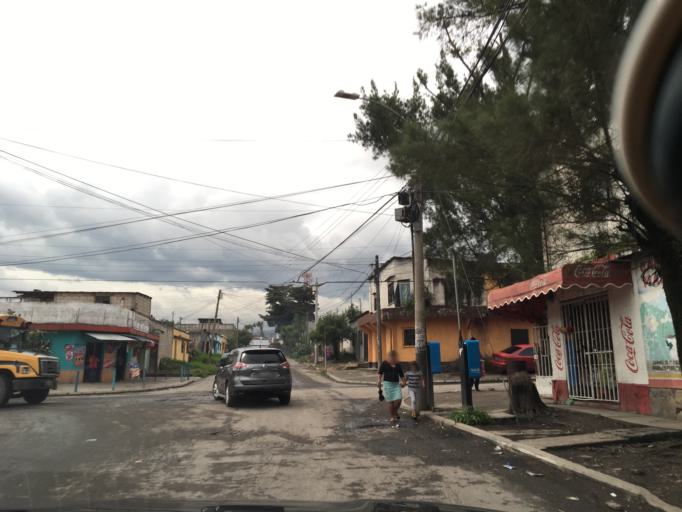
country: GT
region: Guatemala
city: Villa Nueva
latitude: 14.5217
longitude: -90.5734
